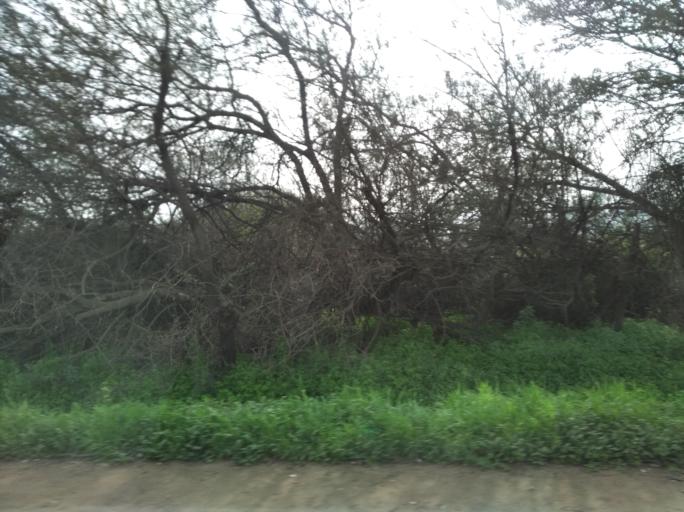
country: CL
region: Santiago Metropolitan
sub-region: Provincia de Chacabuco
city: Lampa
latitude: -33.3035
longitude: -70.8538
